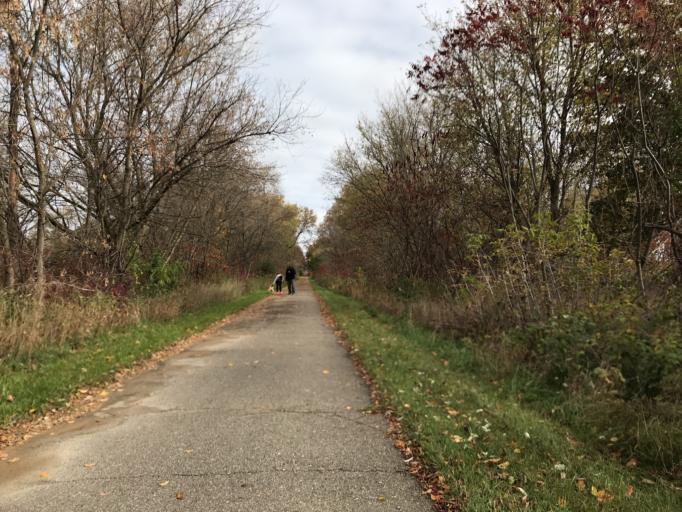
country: US
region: Michigan
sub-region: Oakland County
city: South Lyon
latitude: 42.4870
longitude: -83.6330
